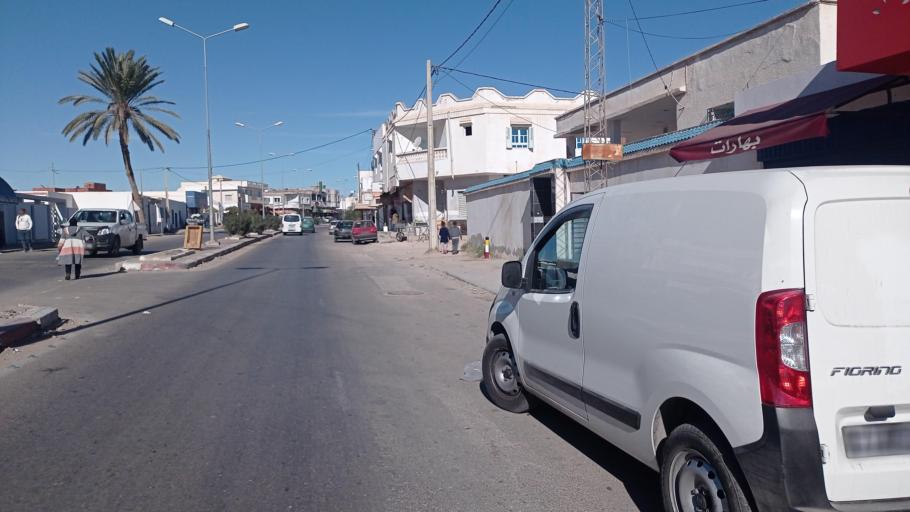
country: TN
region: Qabis
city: Gabes
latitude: 33.8405
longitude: 10.1148
